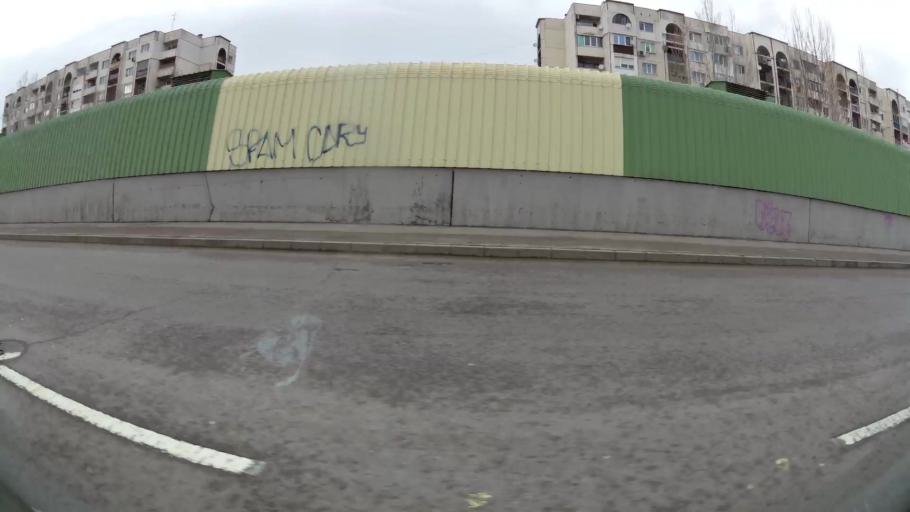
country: BG
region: Sofia-Capital
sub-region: Stolichna Obshtina
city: Sofia
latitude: 42.7384
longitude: 23.2732
